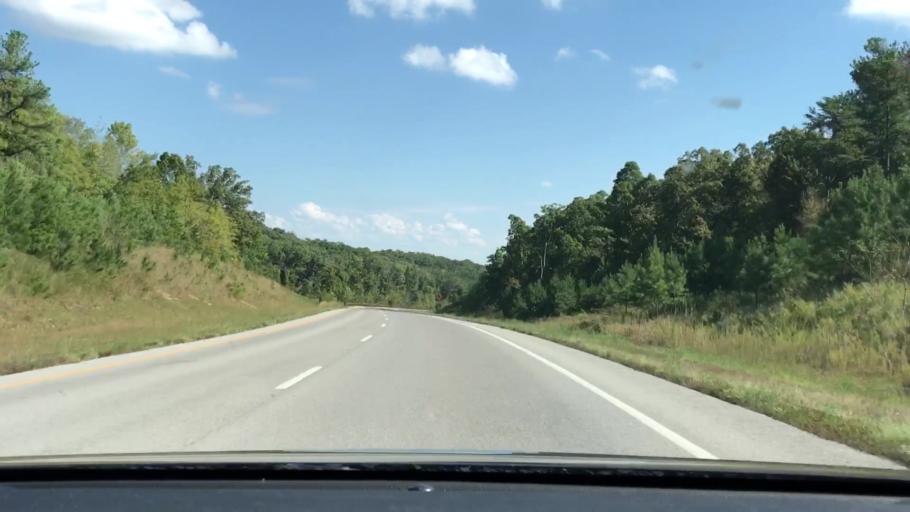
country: US
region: Kentucky
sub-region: Trigg County
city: Cadiz
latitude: 36.7819
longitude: -88.0432
